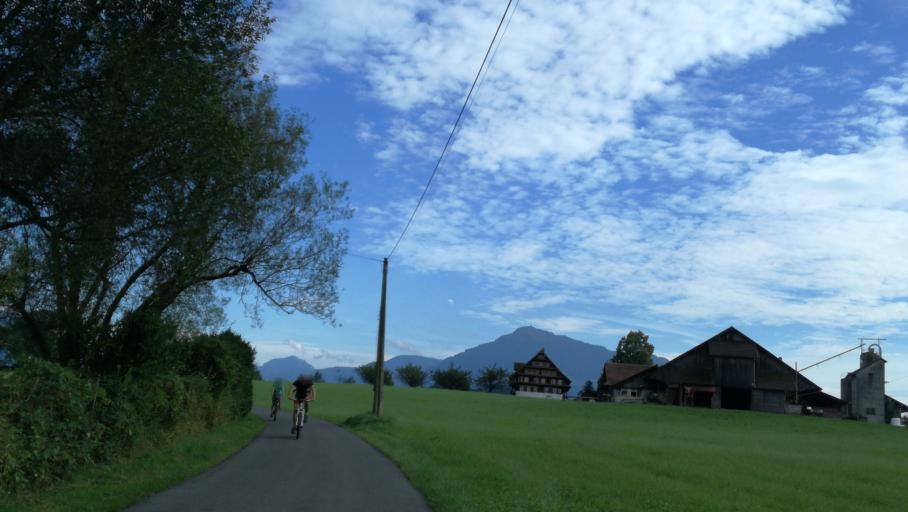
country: CH
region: Zug
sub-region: Zug
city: Cham
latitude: 47.1546
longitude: 8.4526
